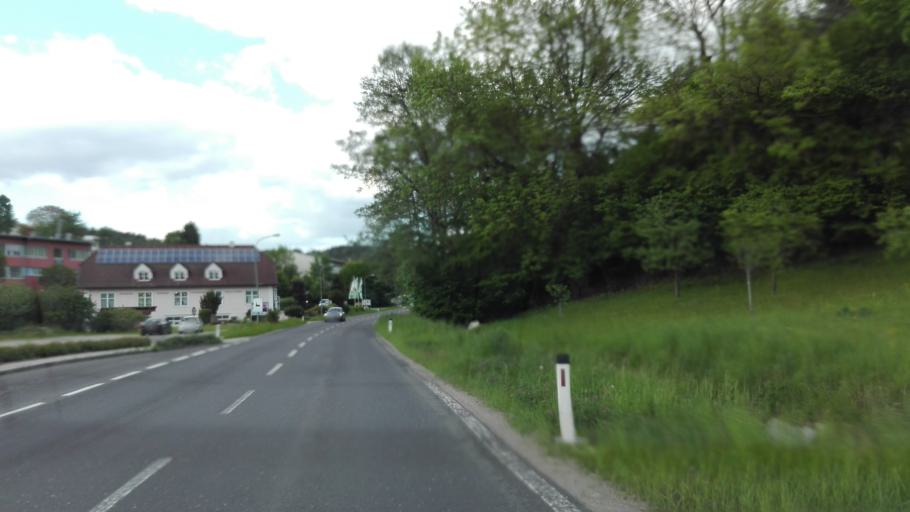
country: AT
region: Upper Austria
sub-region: Politischer Bezirk Perg
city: Bad Kreuzen
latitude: 48.3938
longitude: 14.7305
